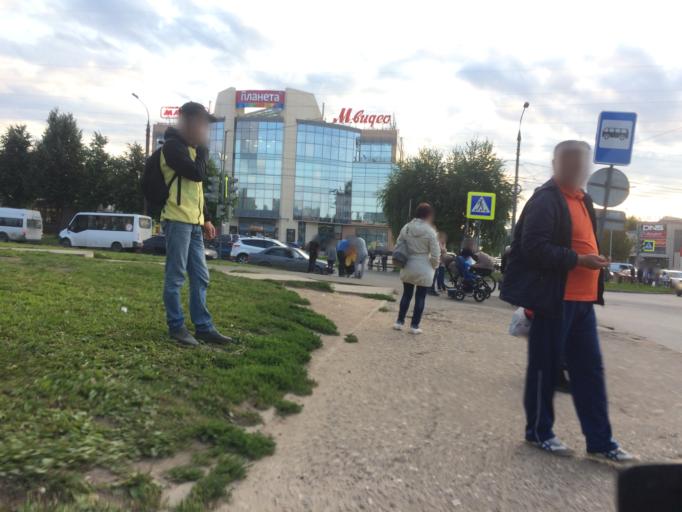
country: RU
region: Mariy-El
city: Medvedevo
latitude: 56.6414
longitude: 47.8455
